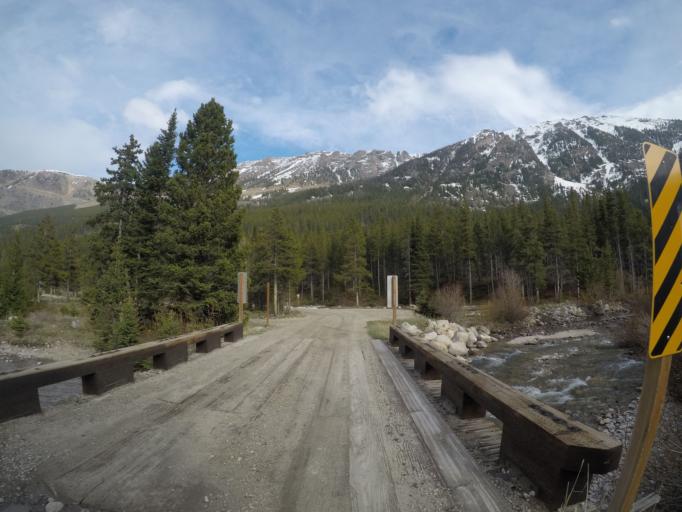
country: US
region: Montana
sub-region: Carbon County
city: Red Lodge
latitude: 45.0280
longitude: -109.4384
